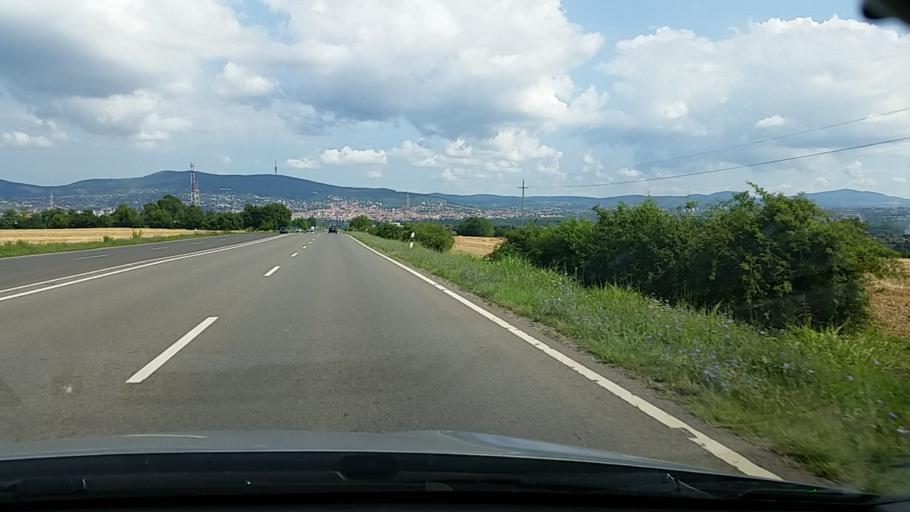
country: HU
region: Baranya
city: Pecs
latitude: 46.0287
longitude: 18.2335
